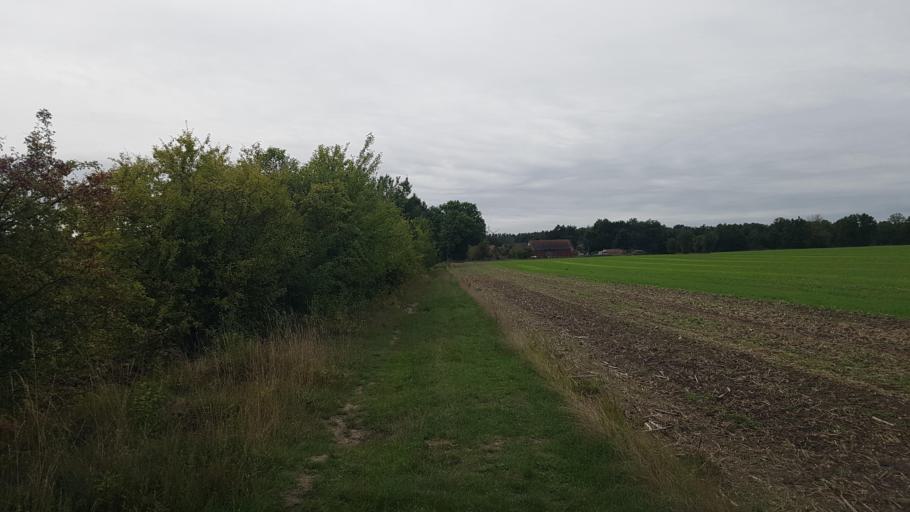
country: DE
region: Brandenburg
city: Schonewalde
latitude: 51.6409
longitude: 13.6057
